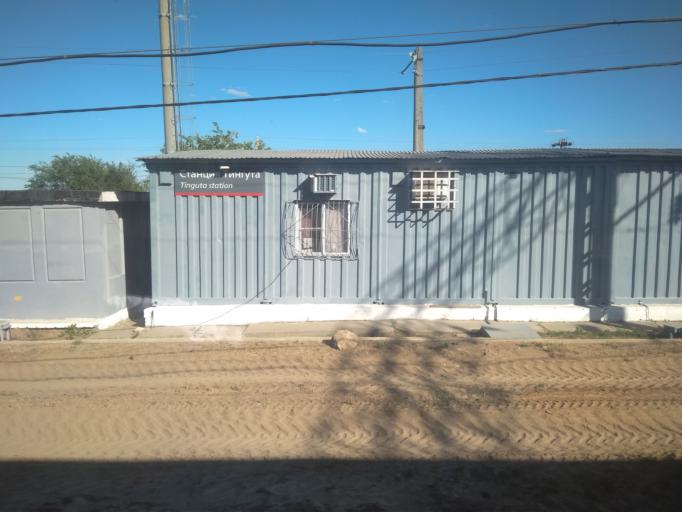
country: RU
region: Volgograd
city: Bereslavka
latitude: 48.2867
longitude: 44.2724
